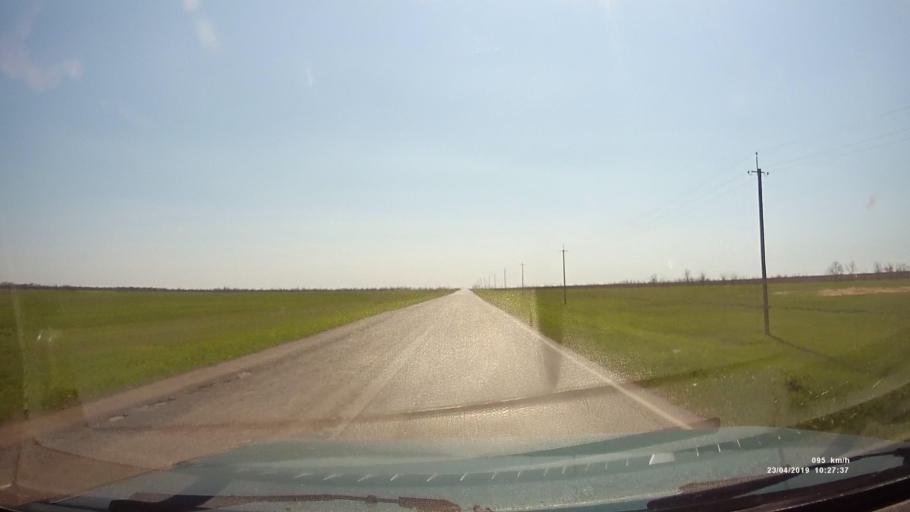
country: RU
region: Kalmykiya
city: Yashalta
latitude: 46.6122
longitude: 42.4941
